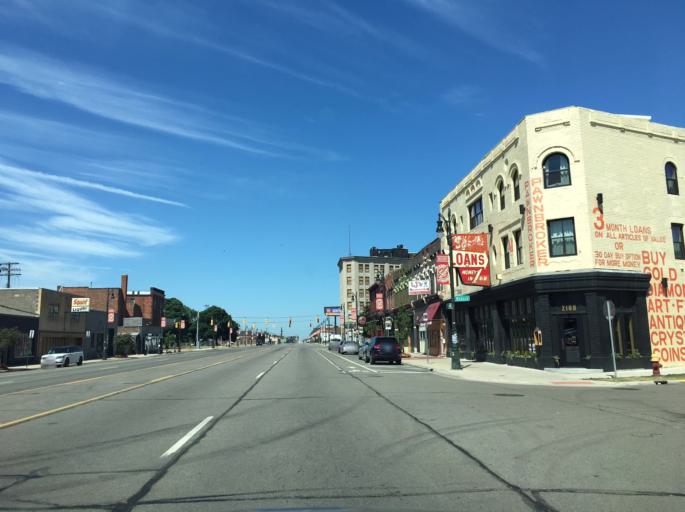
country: US
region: Michigan
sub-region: Wayne County
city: Detroit
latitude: 42.3315
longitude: -83.0749
